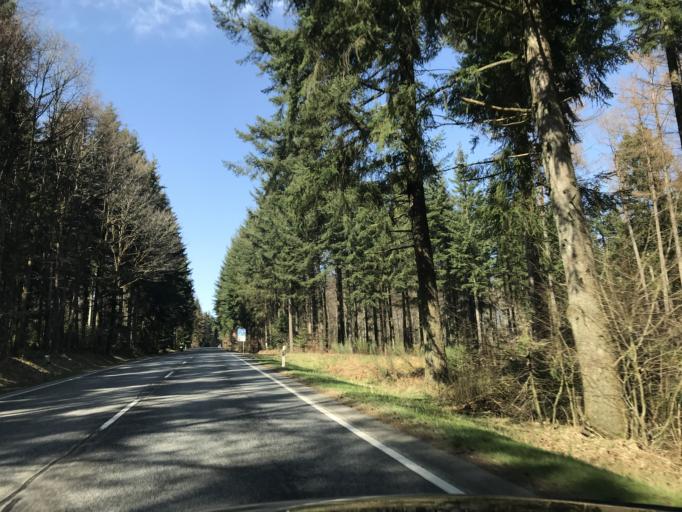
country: DE
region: Saarland
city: Nonnweiler
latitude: 49.6285
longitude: 6.9568
